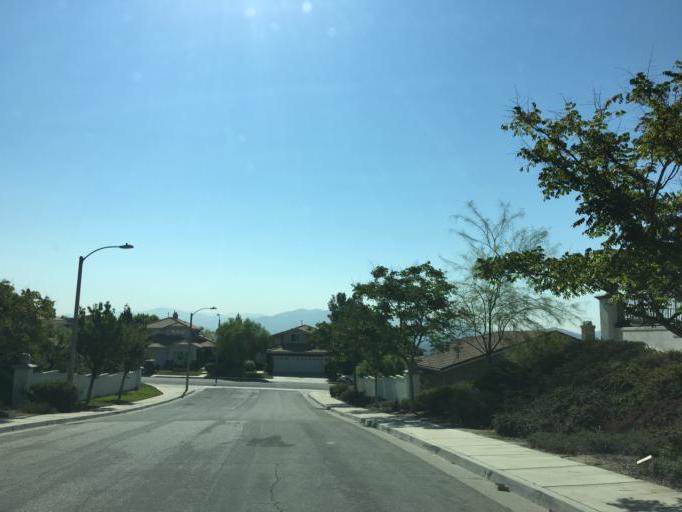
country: US
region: California
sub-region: Los Angeles County
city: Santa Clarita
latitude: 34.3898
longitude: -118.5916
